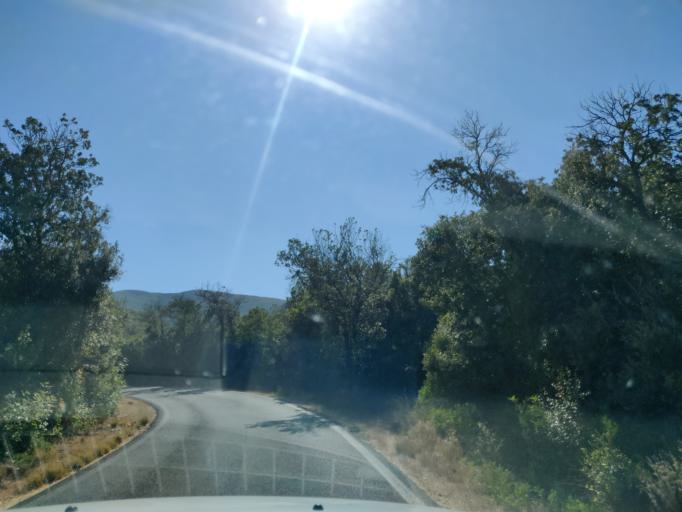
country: IT
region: Tuscany
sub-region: Provincia di Grosseto
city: Porto Ercole
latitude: 42.4247
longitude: 11.1754
